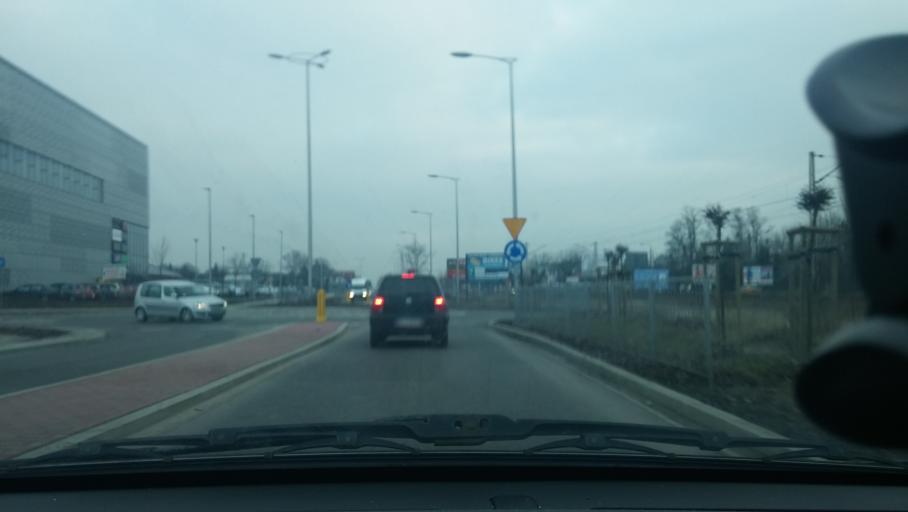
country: PL
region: Masovian Voivodeship
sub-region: Warszawa
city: Wawer
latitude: 52.2072
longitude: 21.1662
